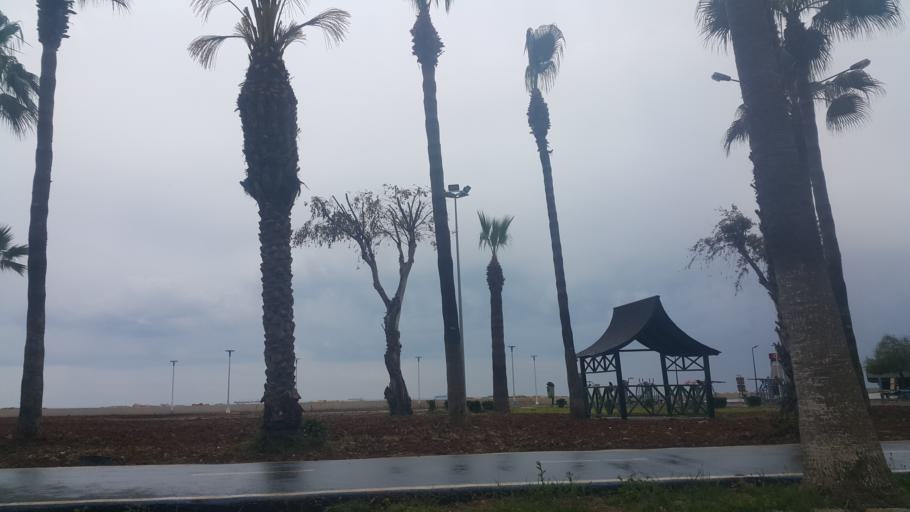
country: TR
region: Mersin
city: Mercin
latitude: 36.7804
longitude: 34.5999
